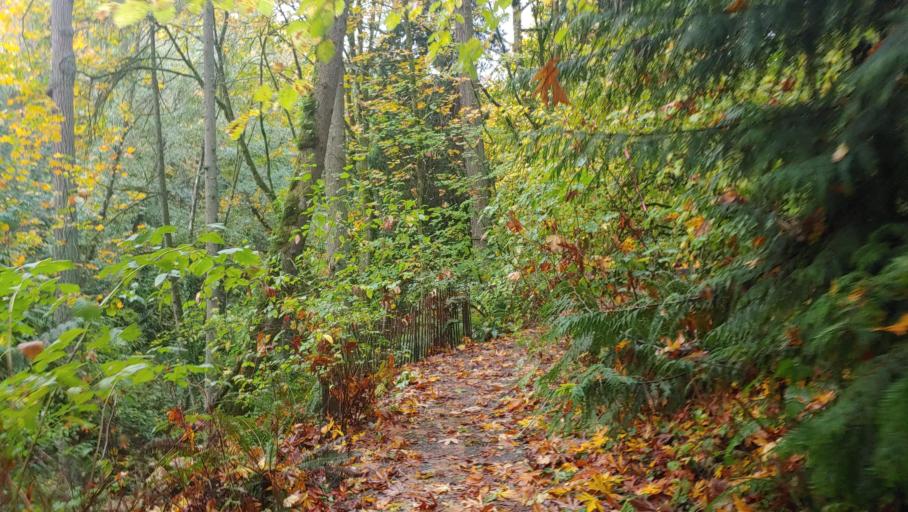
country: US
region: Washington
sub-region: King County
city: Bryn Mawr-Skyway
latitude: 47.5065
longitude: -122.2473
